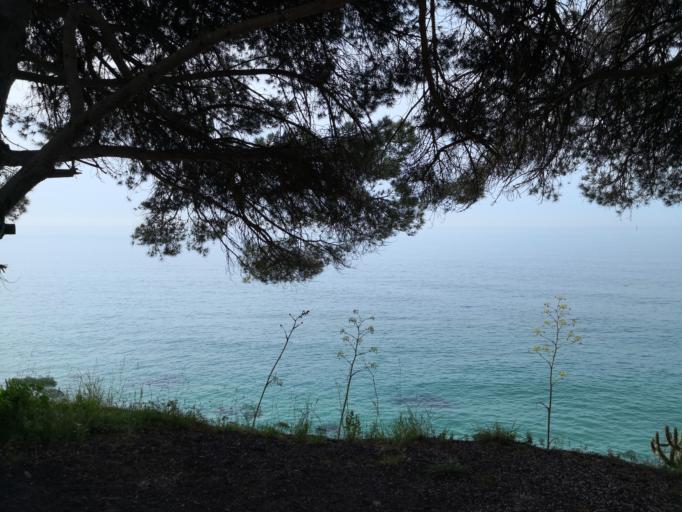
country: PT
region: Setubal
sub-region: Setubal
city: Setubal
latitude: 38.4849
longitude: -8.9567
